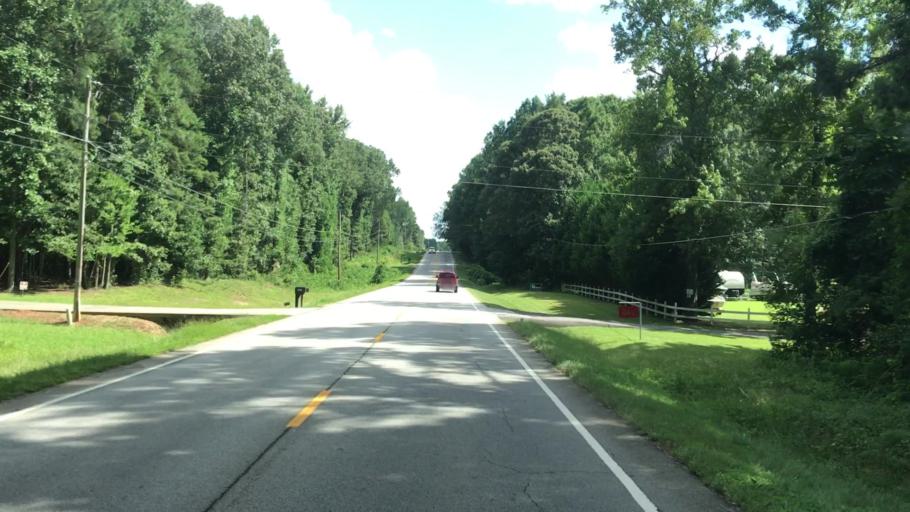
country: US
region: Georgia
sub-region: Walton County
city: Walnut Grove
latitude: 33.7125
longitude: -83.8519
